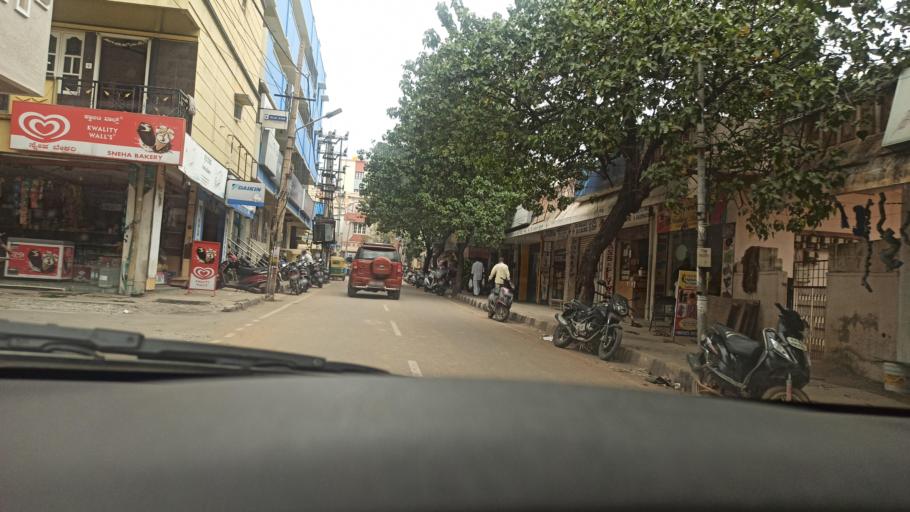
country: IN
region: Karnataka
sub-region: Bangalore Urban
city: Bangalore
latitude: 12.9930
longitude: 77.6801
